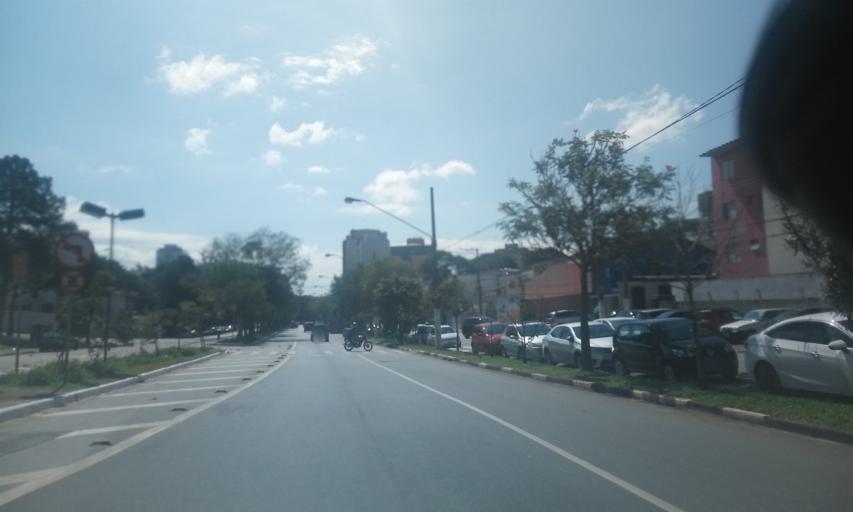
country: BR
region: Sao Paulo
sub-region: Sao Bernardo Do Campo
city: Sao Bernardo do Campo
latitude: -23.6954
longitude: -46.5608
